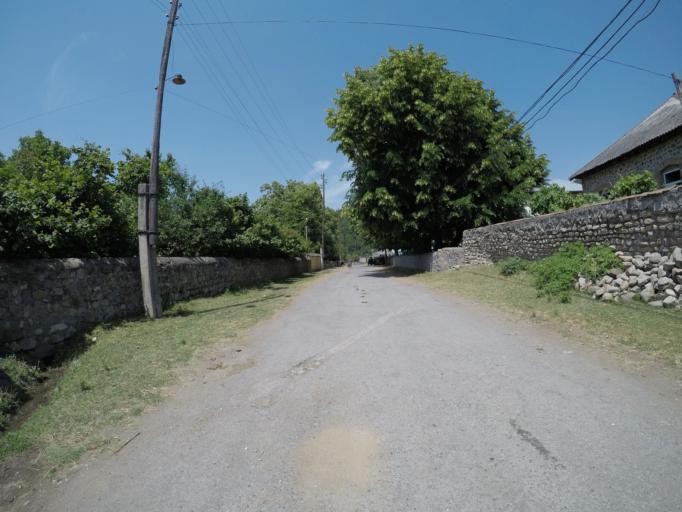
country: AZ
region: Qakh Rayon
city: Cinarli
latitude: 41.4843
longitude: 46.8453
